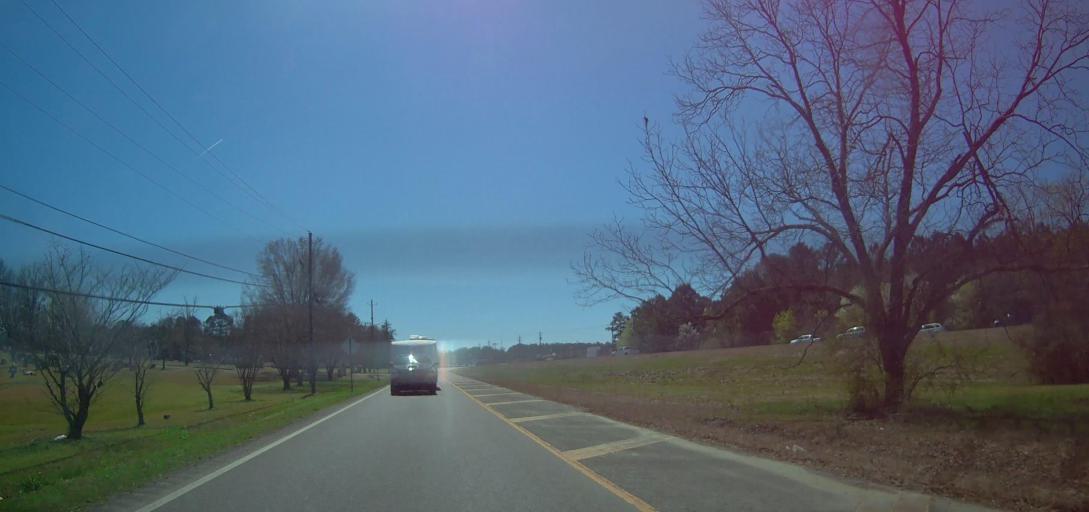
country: US
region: Alabama
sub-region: Etowah County
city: Southside
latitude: 33.9384
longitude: -86.0237
